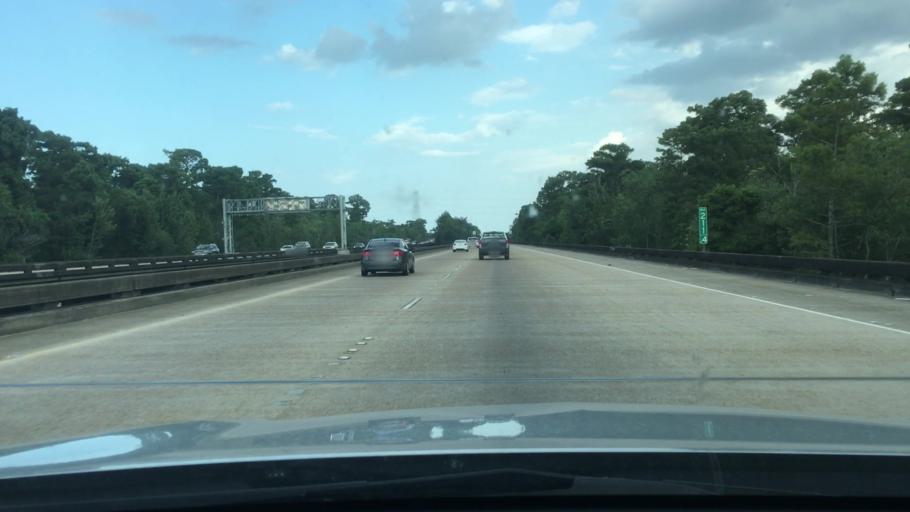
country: US
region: Louisiana
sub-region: Saint John the Baptist Parish
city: Laplace
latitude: 30.0806
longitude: -90.4143
